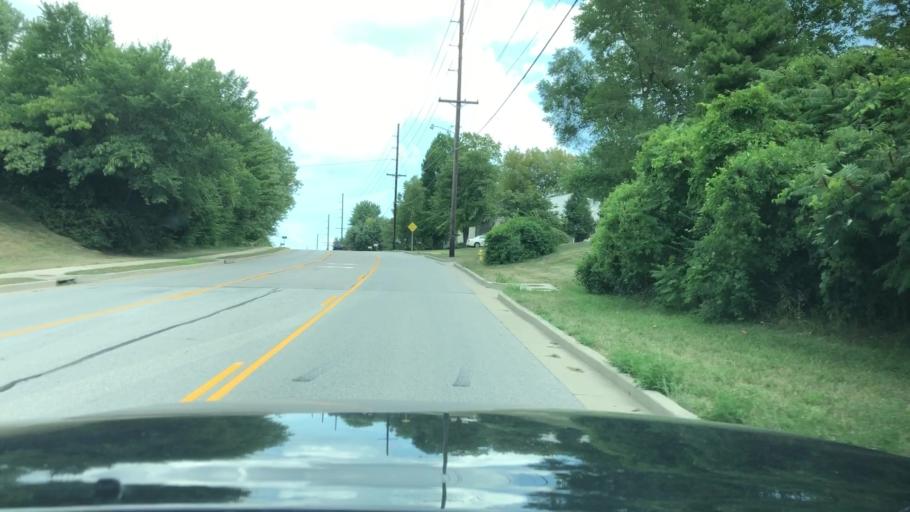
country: US
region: Missouri
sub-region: Saint Charles County
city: Saint Charles
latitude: 38.8061
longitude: -90.5479
